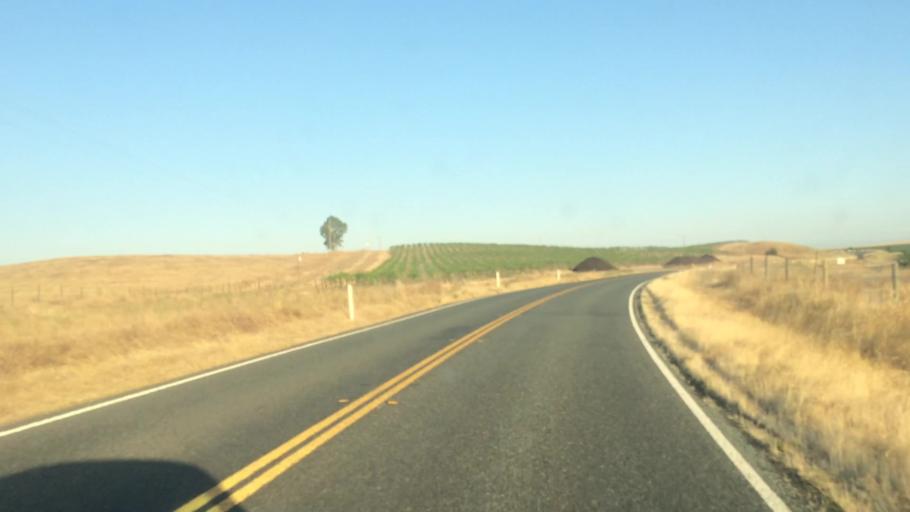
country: US
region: California
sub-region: Sacramento County
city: Clay
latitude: 38.3460
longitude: -121.1138
